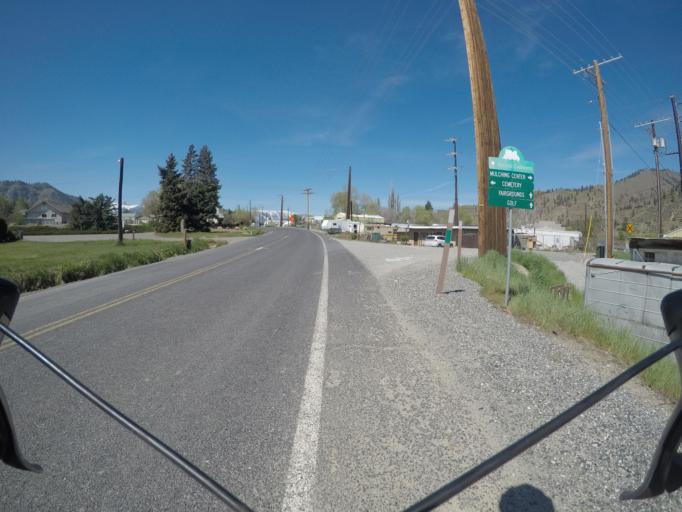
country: US
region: Washington
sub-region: Chelan County
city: Cashmere
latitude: 47.5242
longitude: -120.4855
